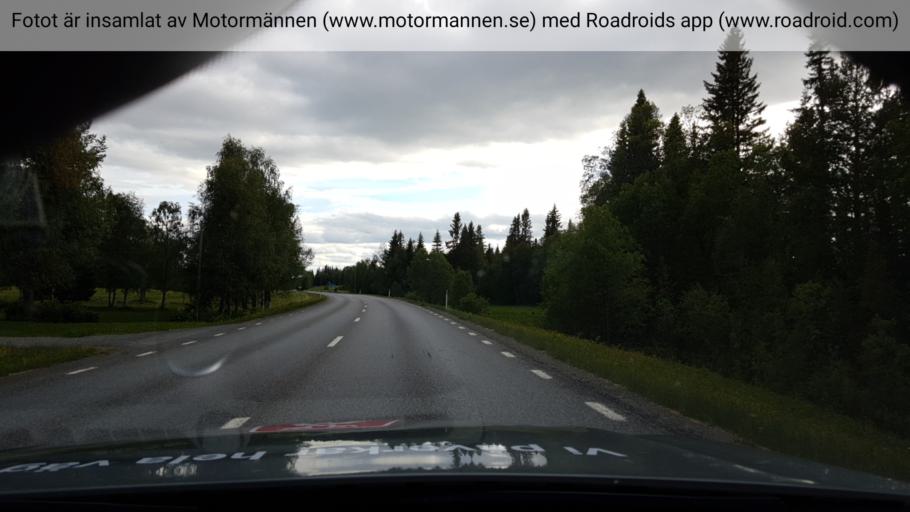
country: SE
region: Jaemtland
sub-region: OEstersunds Kommun
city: Lit
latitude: 63.4375
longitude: 15.1261
